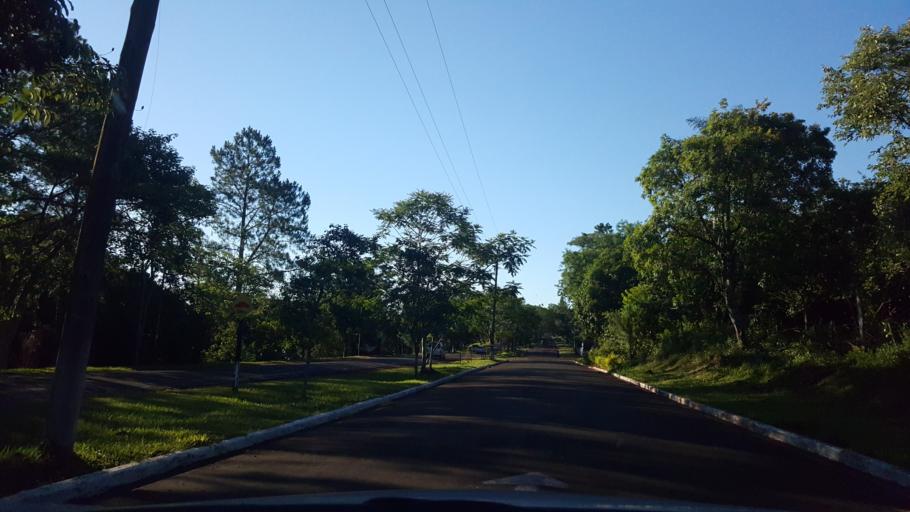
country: AR
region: Misiones
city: Gobernador Roca
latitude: -27.1324
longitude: -55.5074
